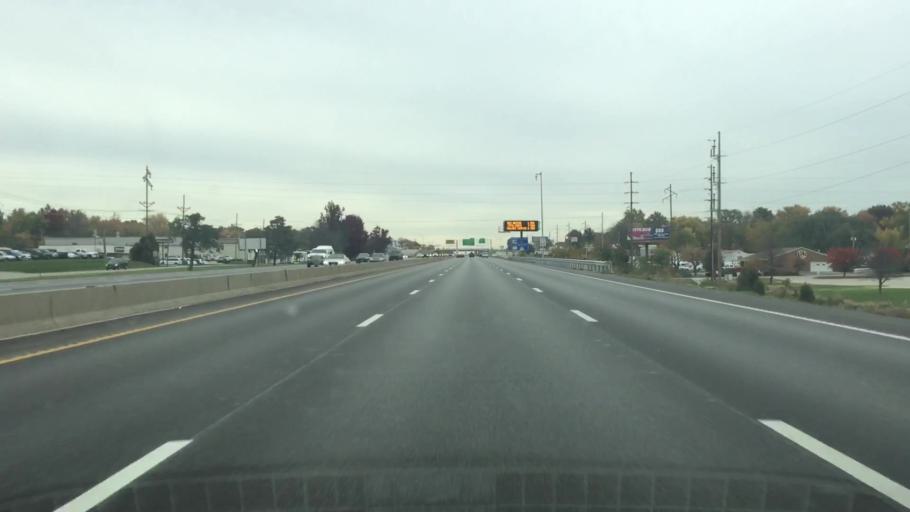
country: US
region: Missouri
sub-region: Jackson County
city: Grandview
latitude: 38.8780
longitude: -94.5258
